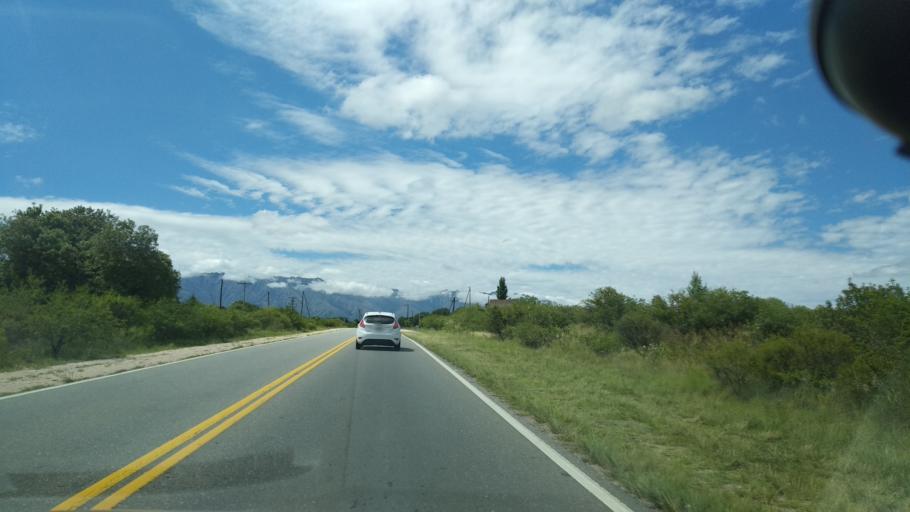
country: AR
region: Cordoba
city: Mina Clavero
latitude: -31.7607
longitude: -64.9714
